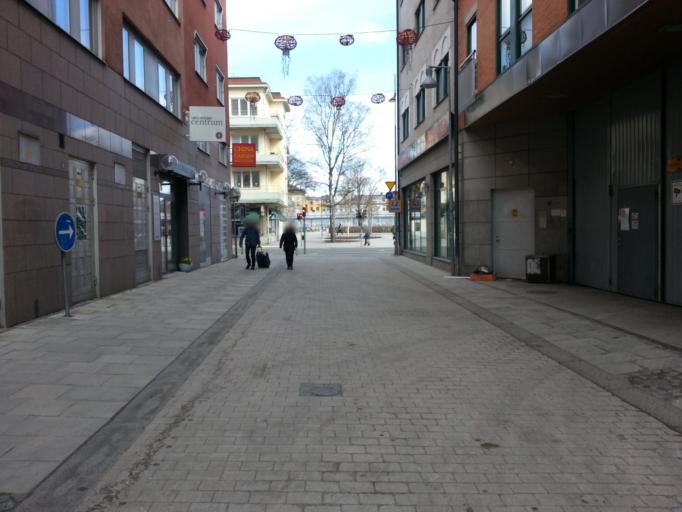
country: SE
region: Uppsala
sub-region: Uppsala Kommun
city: Uppsala
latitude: 59.8586
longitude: 17.6430
